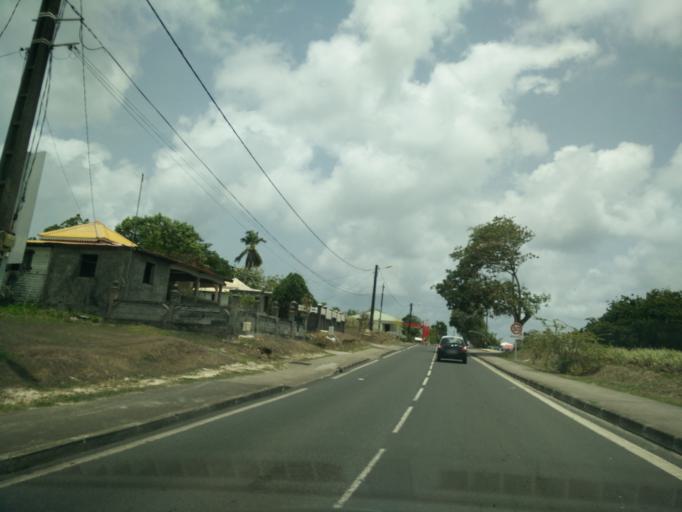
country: GP
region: Guadeloupe
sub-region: Guadeloupe
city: Port-Louis
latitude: 16.4149
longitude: -61.5196
